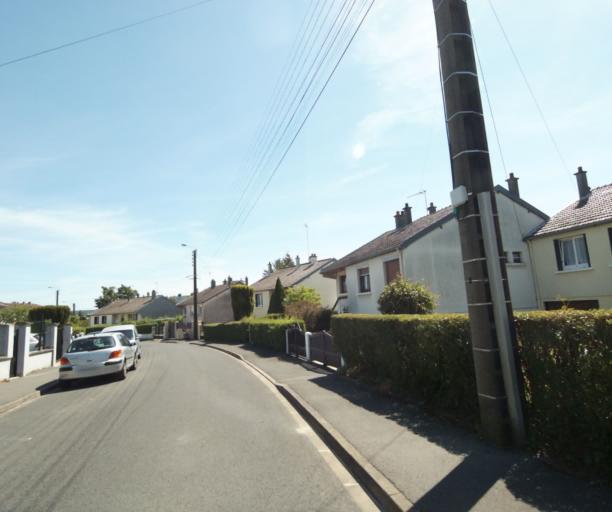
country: FR
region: Champagne-Ardenne
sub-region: Departement des Ardennes
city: La Francheville
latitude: 49.7464
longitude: 4.7160
